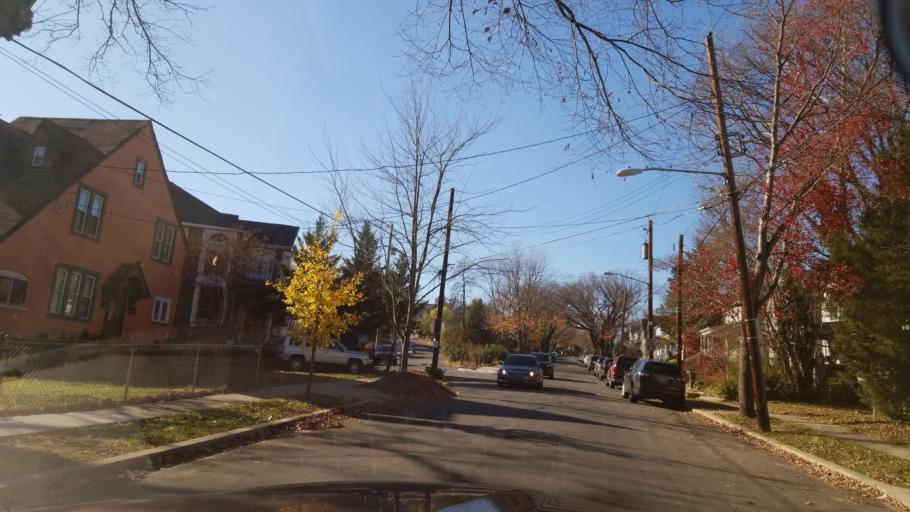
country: US
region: Maryland
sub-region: Prince George's County
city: Mount Rainier
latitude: 38.9329
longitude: -76.9648
